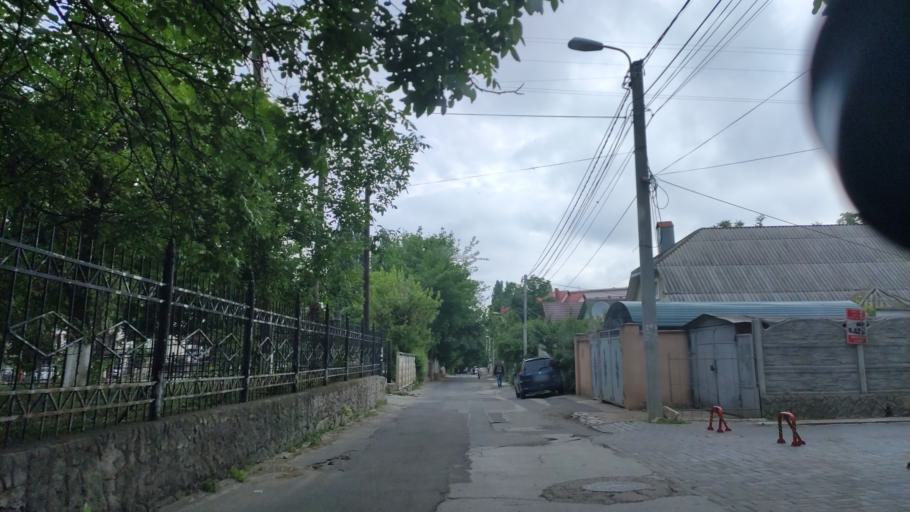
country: MD
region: Chisinau
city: Chisinau
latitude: 46.9853
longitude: 28.8712
